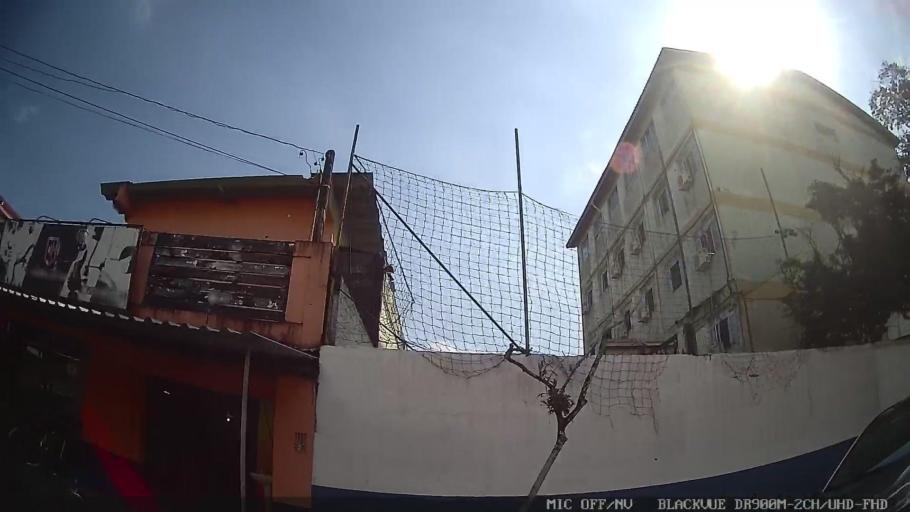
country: BR
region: Sao Paulo
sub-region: Santos
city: Santos
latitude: -23.9409
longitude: -46.3026
